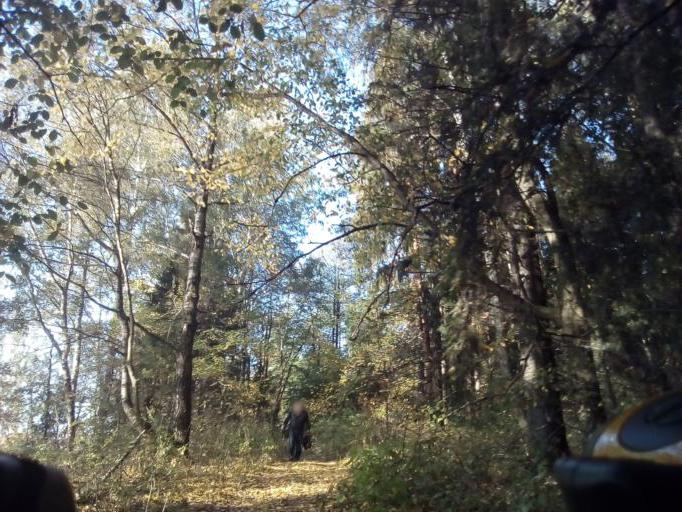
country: RU
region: Moskovskaya
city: Gzhel'
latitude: 55.5878
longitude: 38.3243
